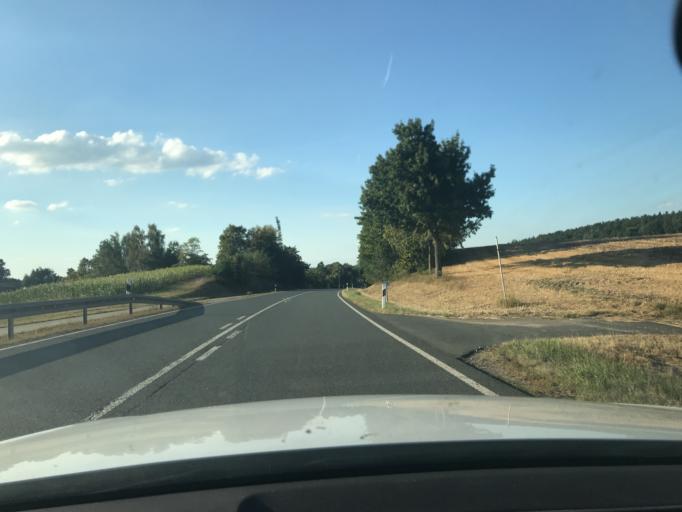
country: DE
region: Bavaria
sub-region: Upper Franconia
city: Emtmannsberg
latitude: 49.9011
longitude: 11.6087
